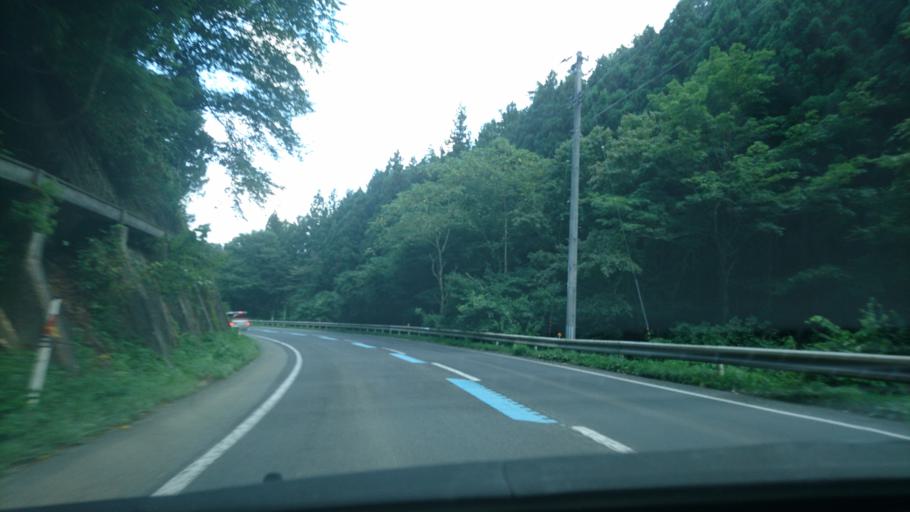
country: JP
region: Iwate
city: Mizusawa
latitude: 39.0414
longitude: 141.2436
